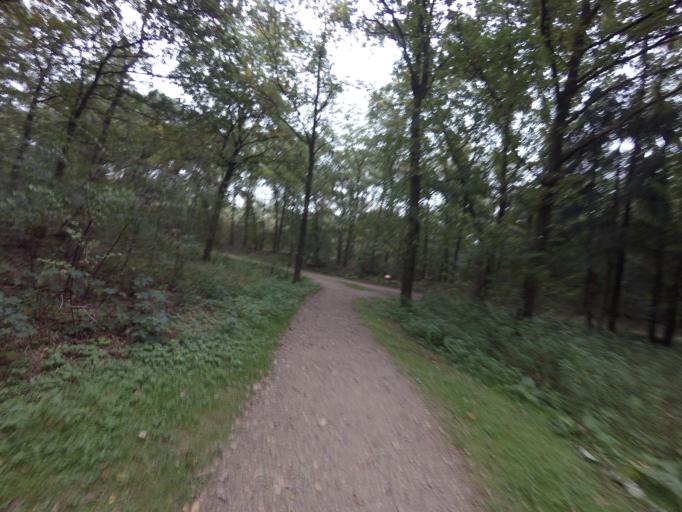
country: NL
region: North Holland
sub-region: Gemeente Hilversum
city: Hilversum
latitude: 52.2017
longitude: 5.2027
